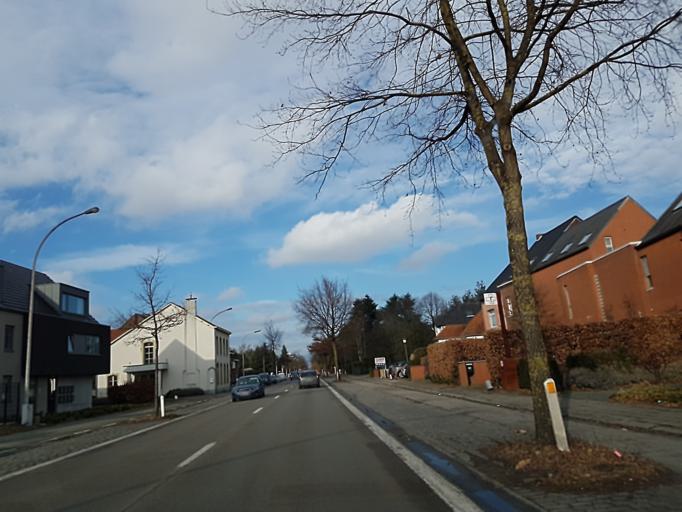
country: BE
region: Flanders
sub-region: Provincie Antwerpen
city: Mol
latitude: 51.1971
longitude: 5.1156
